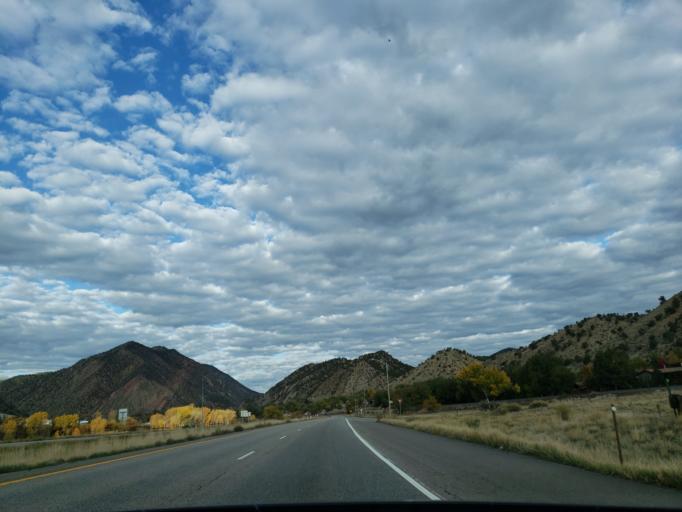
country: US
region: Colorado
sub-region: Garfield County
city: New Castle
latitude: 39.5669
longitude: -107.5194
